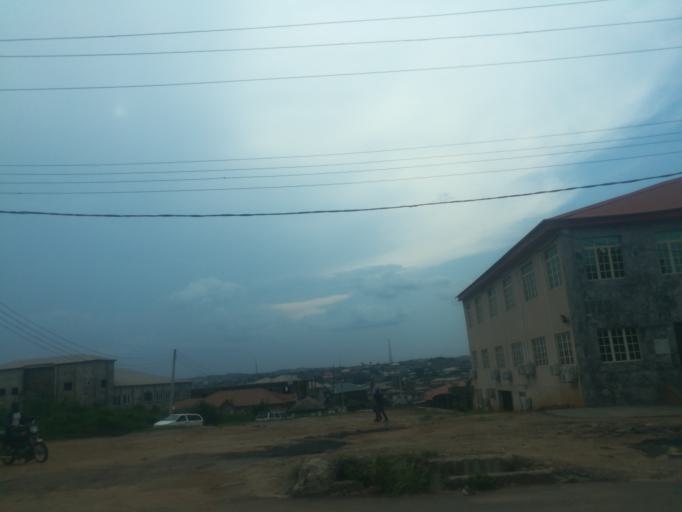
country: NG
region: Oyo
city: Ibadan
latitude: 7.3757
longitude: 3.8287
